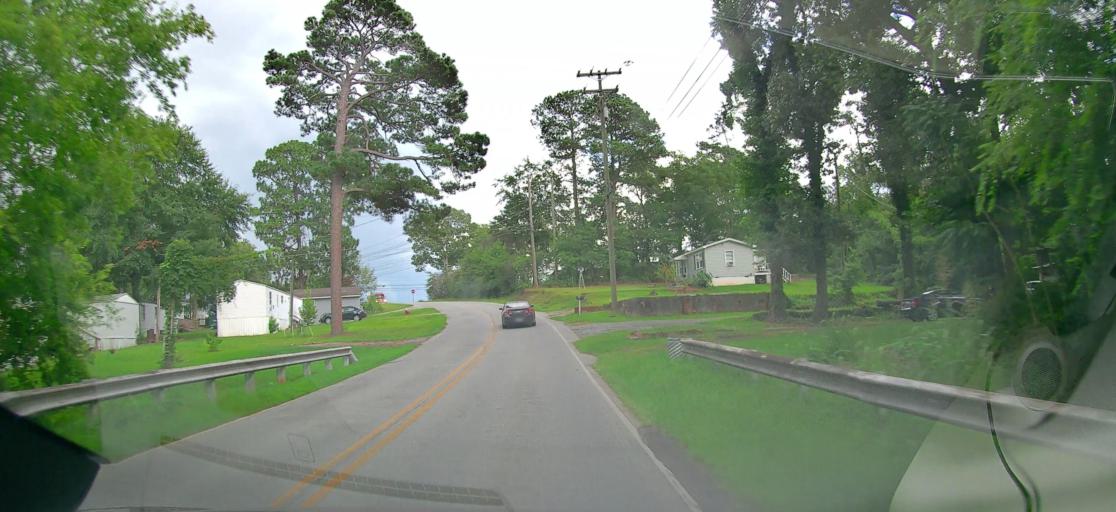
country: US
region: Georgia
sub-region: Houston County
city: Centerville
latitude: 32.6308
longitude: -83.6815
